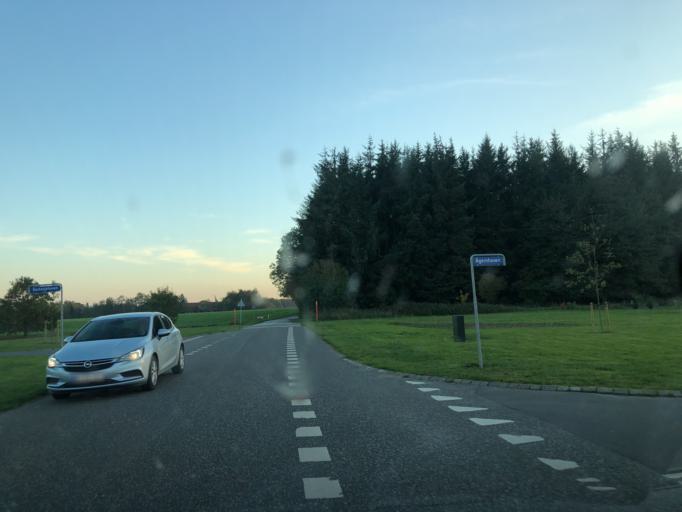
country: DK
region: South Denmark
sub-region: Vejle Kommune
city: Borkop
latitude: 55.6291
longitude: 9.6485
